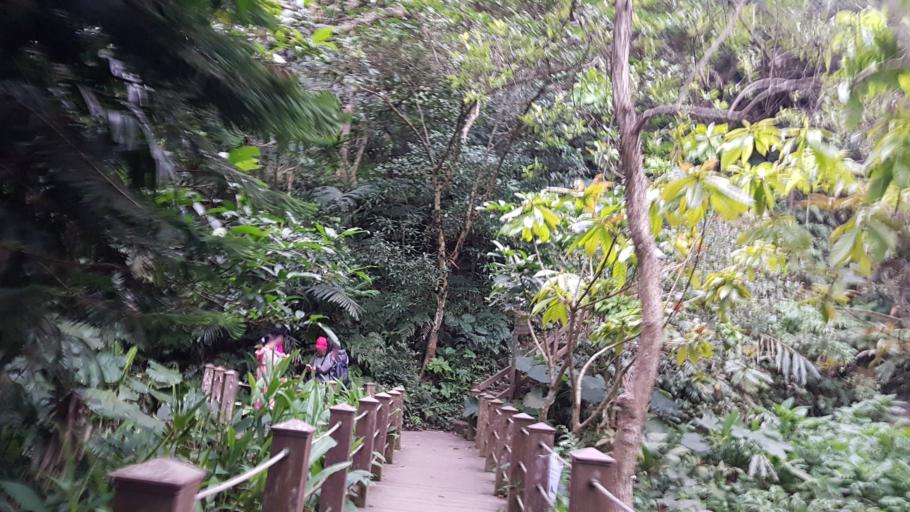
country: TW
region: Taipei
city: Taipei
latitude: 25.0152
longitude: 121.5575
